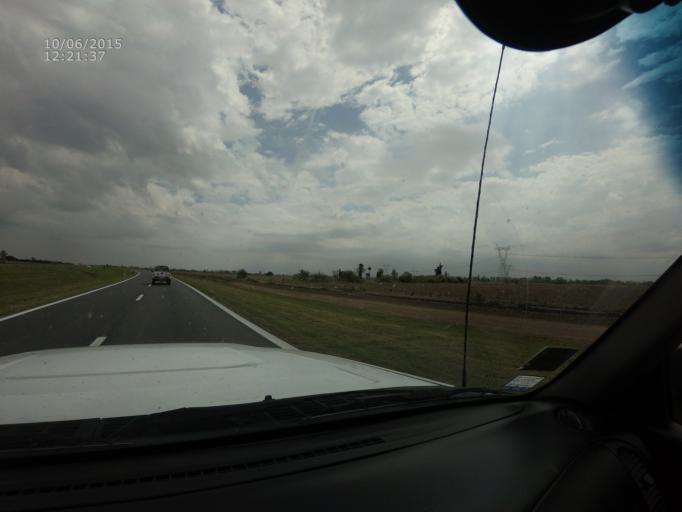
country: AR
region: Santa Fe
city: Roldan
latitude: -32.9211
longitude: -60.9203
